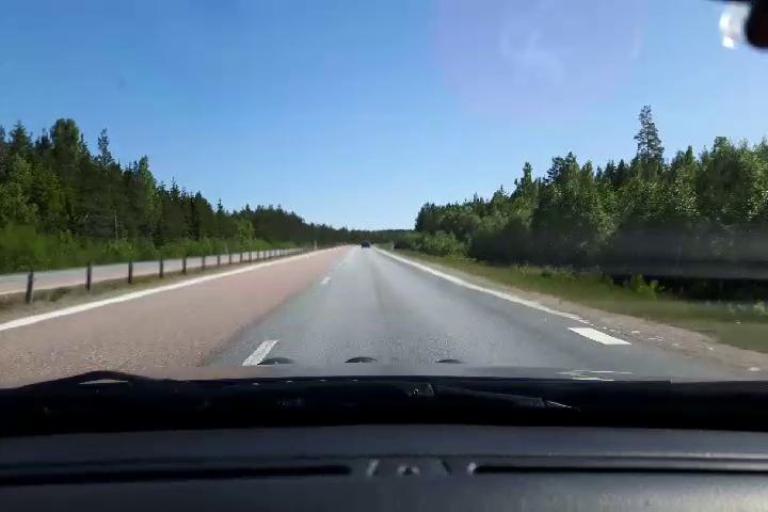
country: SE
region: Gaevleborg
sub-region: Soderhamns Kommun
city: Soderhamn
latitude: 61.4132
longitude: 16.9904
